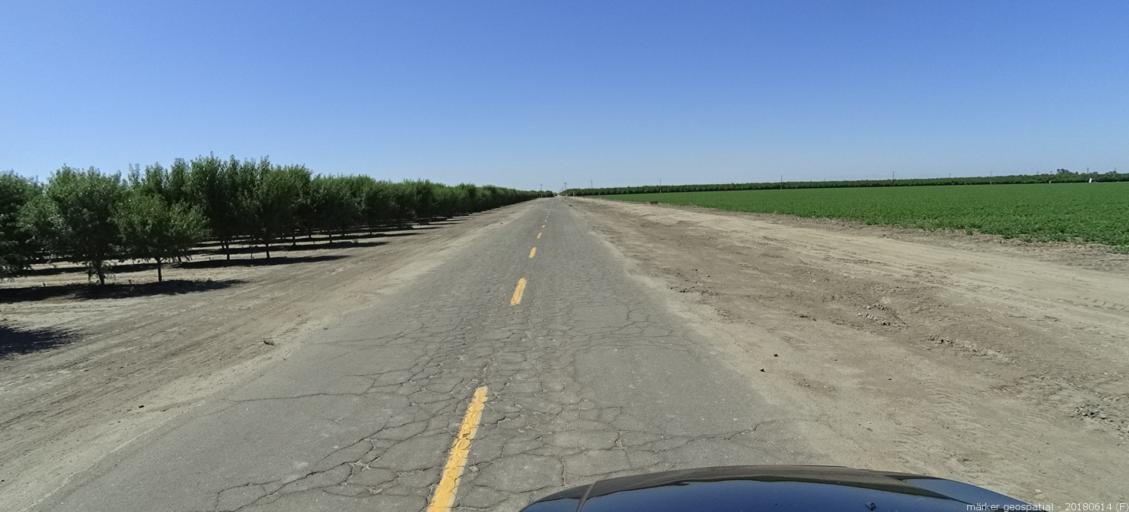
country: US
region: California
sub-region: Madera County
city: Fairmead
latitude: 36.9563
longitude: -120.2202
